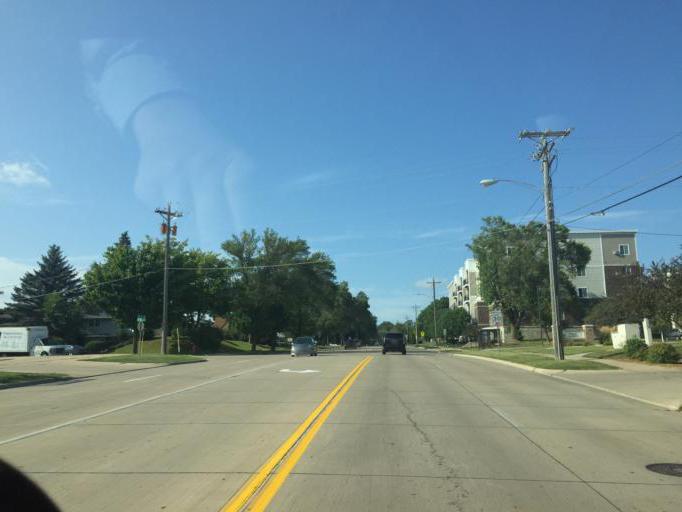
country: US
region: Minnesota
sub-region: Olmsted County
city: Rochester
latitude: 44.0316
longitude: -92.4790
